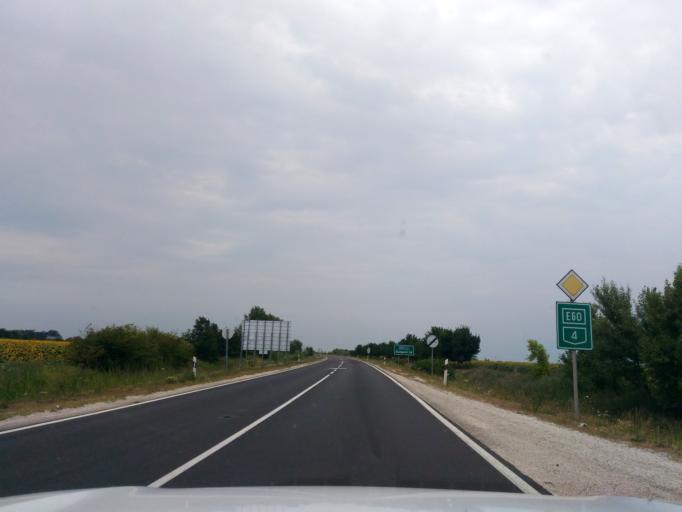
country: HU
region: Jasz-Nagykun-Szolnok
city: Zagyvarekas
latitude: 47.1855
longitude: 20.0966
